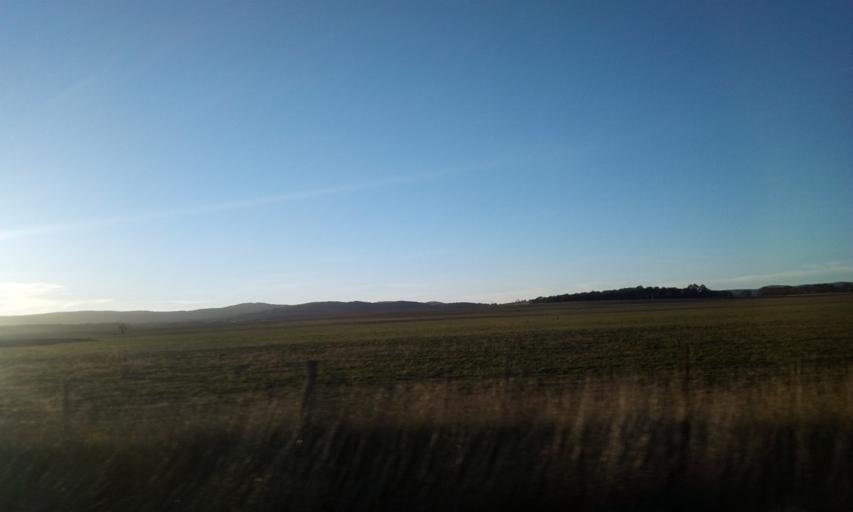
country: AU
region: New South Wales
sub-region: Goulburn Mulwaree
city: Goulburn
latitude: -34.8553
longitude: 149.5527
